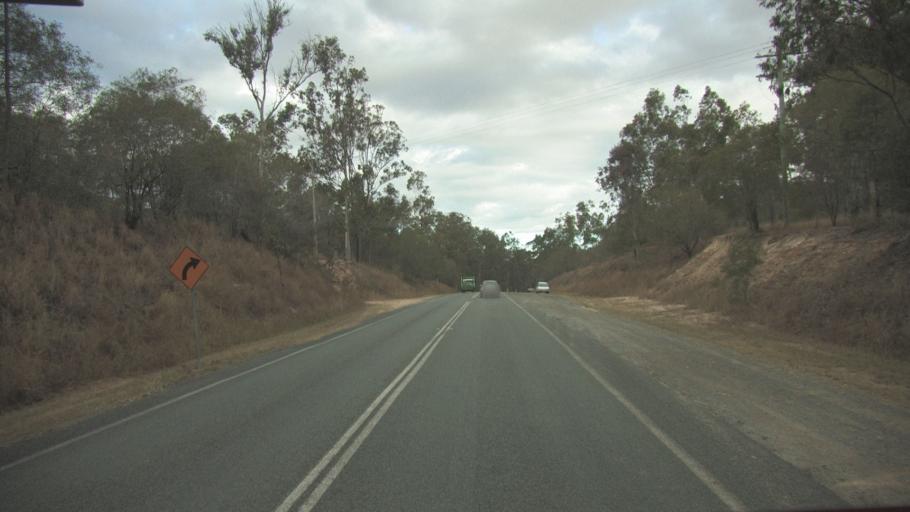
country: AU
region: Queensland
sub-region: Logan
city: Cedar Vale
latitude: -27.9002
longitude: 153.0899
